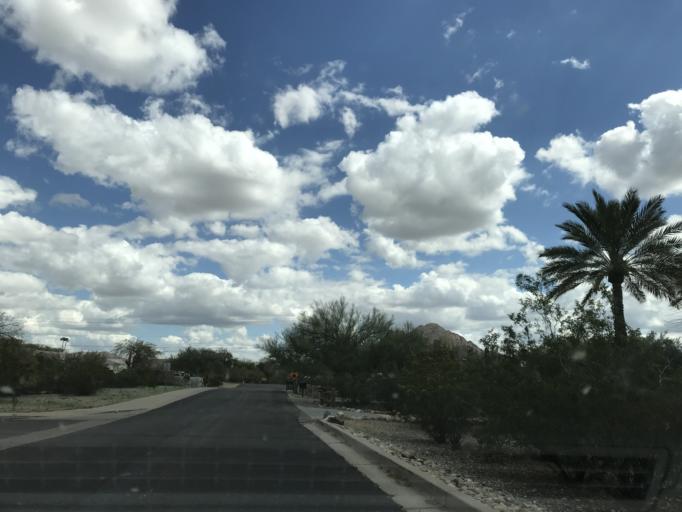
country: US
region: Arizona
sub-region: Maricopa County
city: Paradise Valley
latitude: 33.5245
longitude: -112.0008
